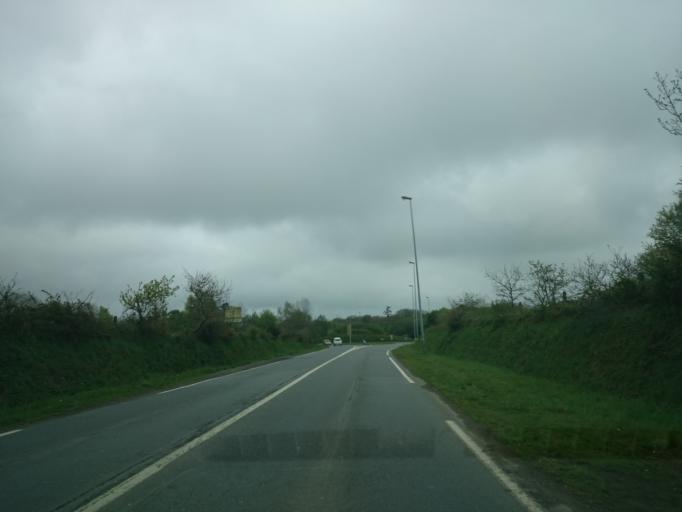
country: FR
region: Brittany
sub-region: Departement du Finistere
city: Gouesnou
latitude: 48.4449
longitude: -4.4584
